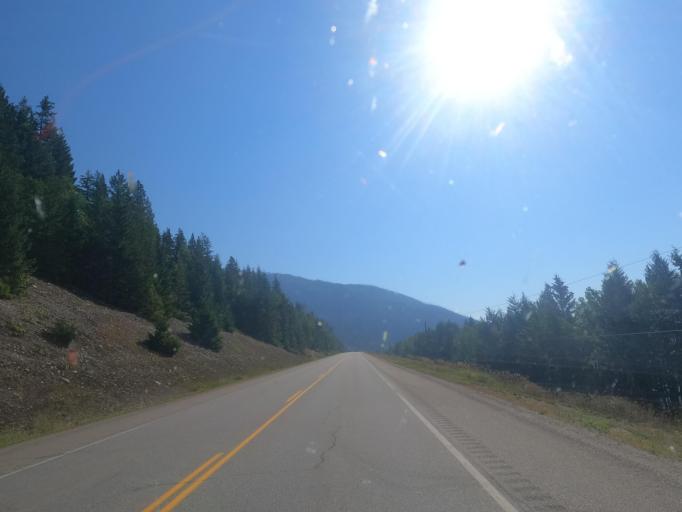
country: CA
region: Alberta
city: Jasper Park Lodge
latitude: 52.9547
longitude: -118.8853
